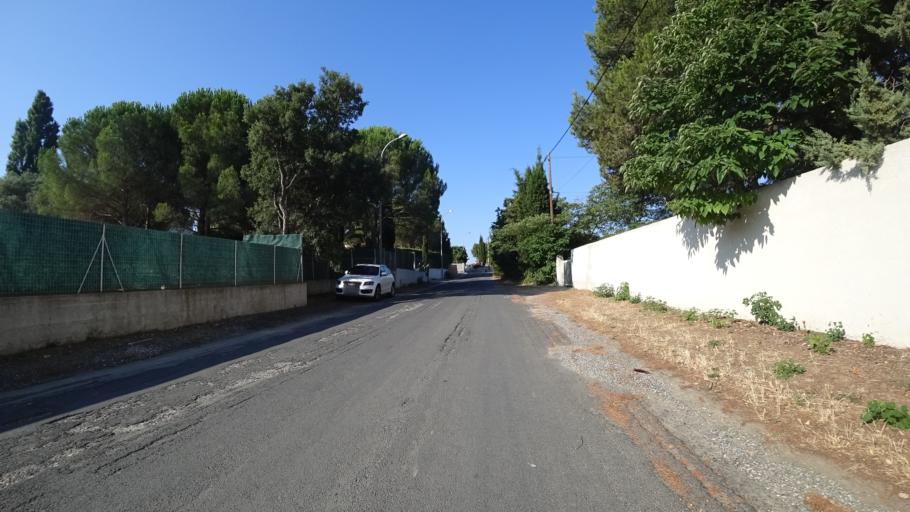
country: FR
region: Languedoc-Roussillon
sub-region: Departement des Pyrenees-Orientales
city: Cabestany
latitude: 42.6946
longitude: 2.9704
